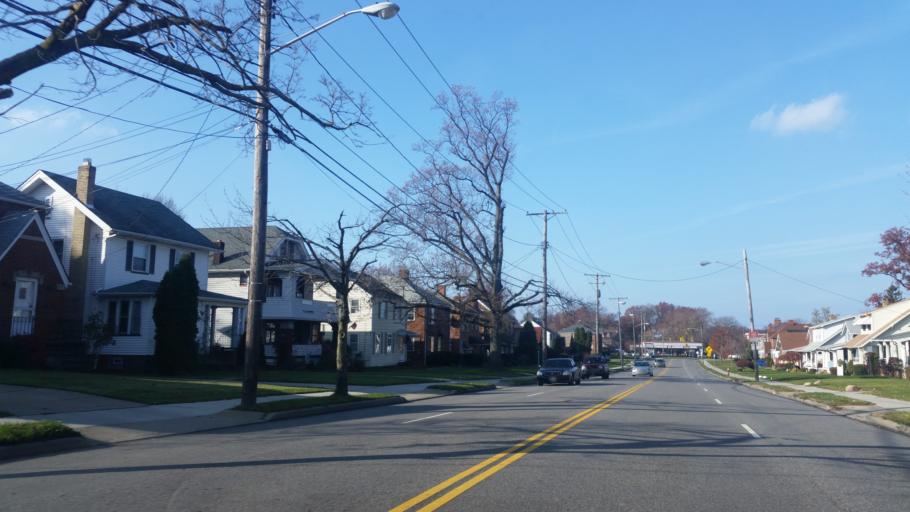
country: US
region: Ohio
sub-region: Cuyahoga County
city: Lakewood
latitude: 41.4567
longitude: -81.8032
